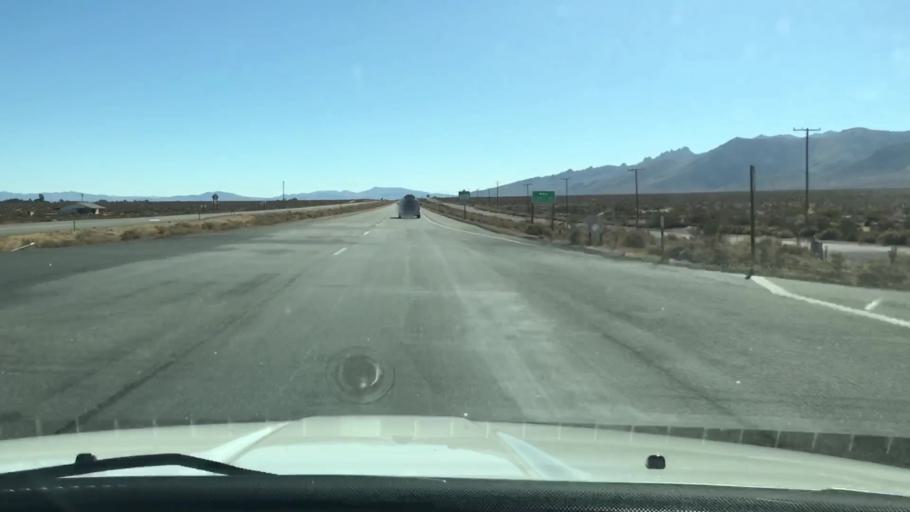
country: US
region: California
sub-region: Kern County
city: Inyokern
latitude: 35.7984
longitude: -117.8729
